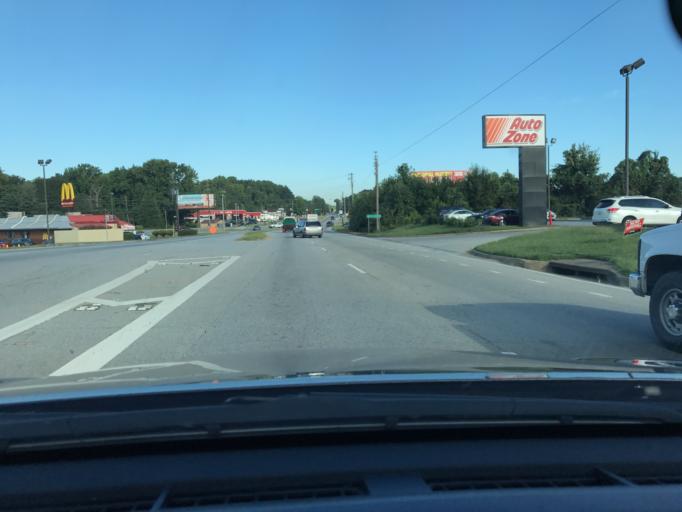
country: US
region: Georgia
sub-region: Clayton County
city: Lake City
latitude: 33.6134
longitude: -84.3470
